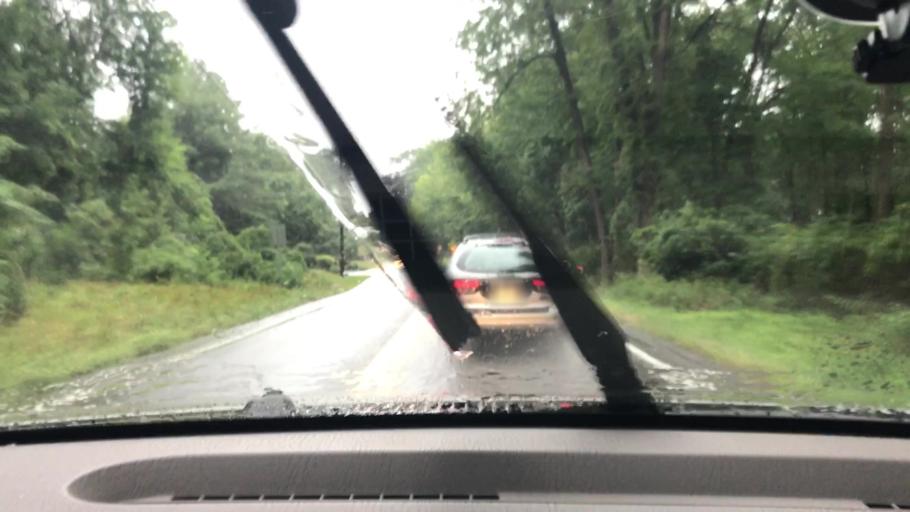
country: US
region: Pennsylvania
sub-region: Lancaster County
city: Elizabethtown
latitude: 40.1467
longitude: -76.6220
